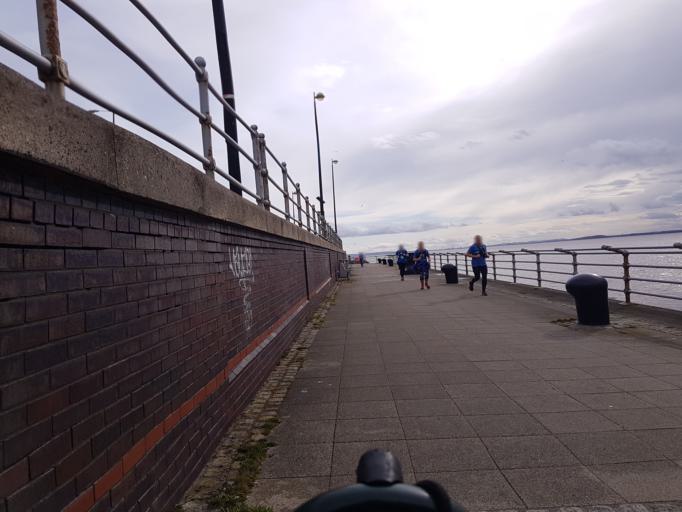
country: GB
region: England
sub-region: Metropolitan Borough of Wirral
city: Bromborough
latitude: 53.3745
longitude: -2.9655
